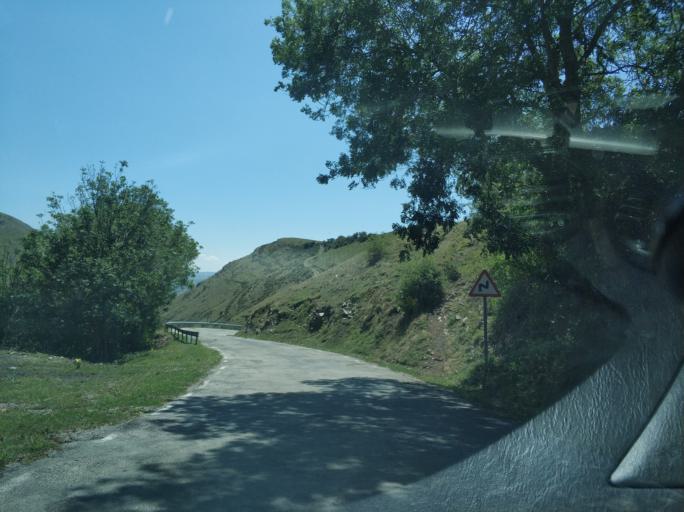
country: ES
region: Cantabria
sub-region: Provincia de Cantabria
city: Reinosa
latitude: 43.0334
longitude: -4.1726
